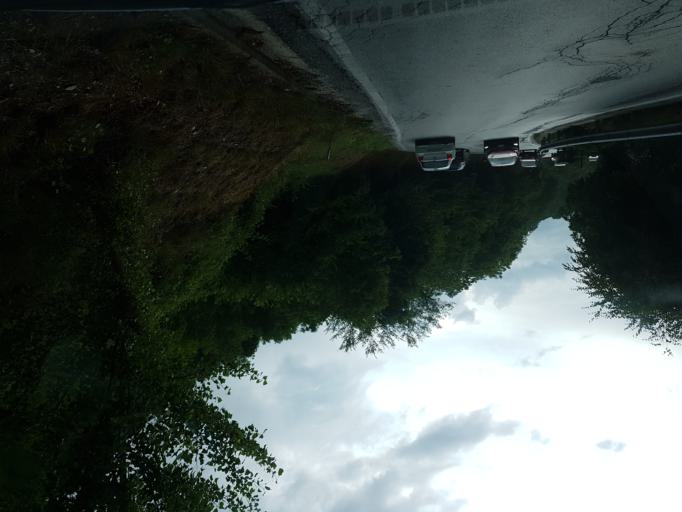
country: IT
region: Piedmont
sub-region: Provincia di Cuneo
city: Macra
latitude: 44.4986
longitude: 7.1860
